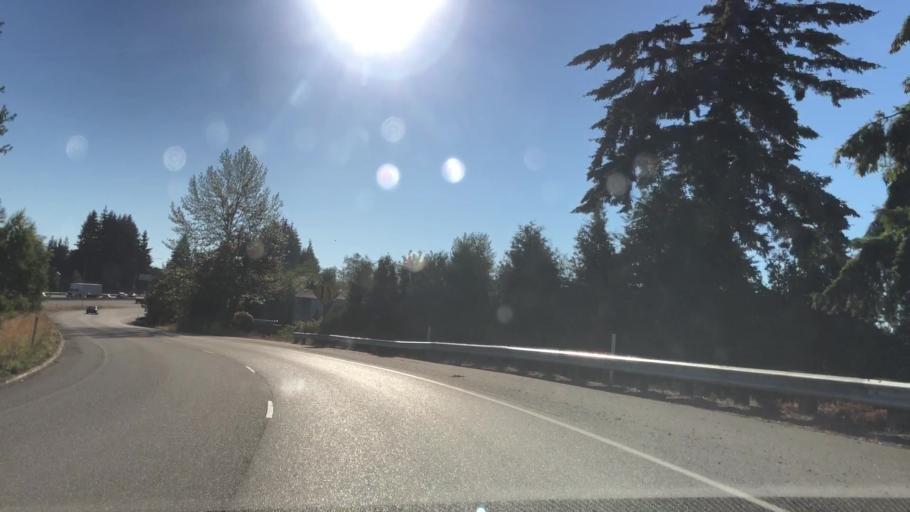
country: US
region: Washington
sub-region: Snohomish County
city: Mukilteo
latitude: 47.9220
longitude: -122.2596
